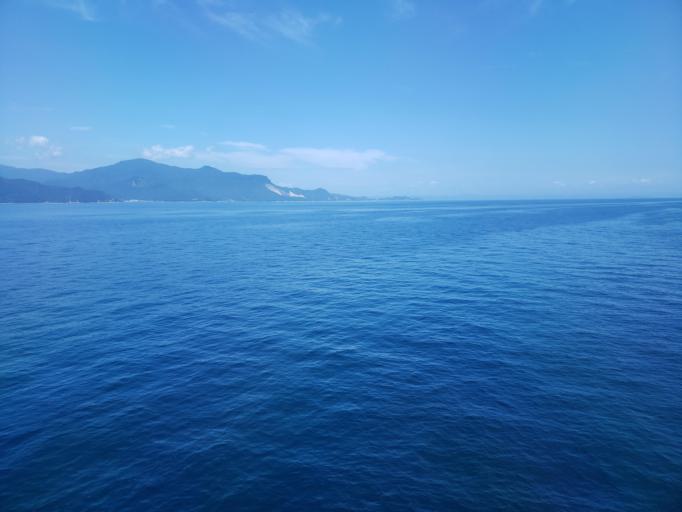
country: JP
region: Kagawa
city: Tonosho
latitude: 34.4393
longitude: 134.3951
